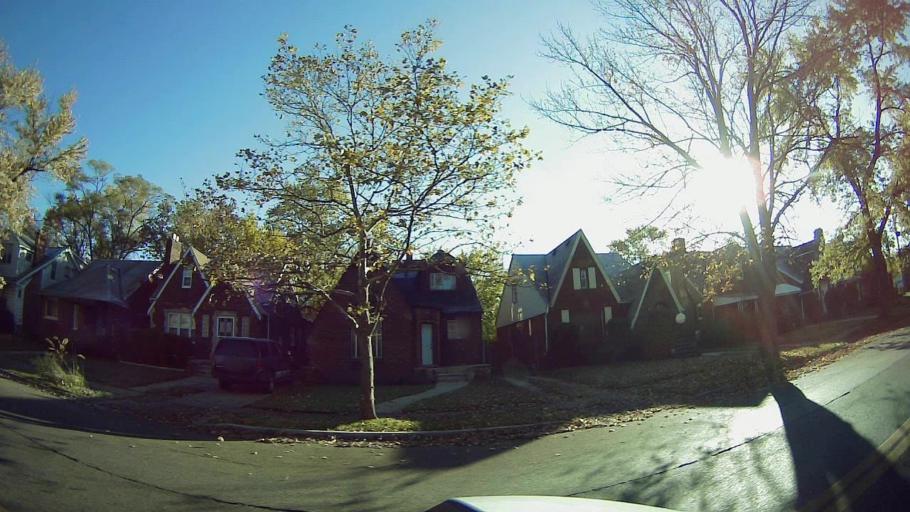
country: US
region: Michigan
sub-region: Wayne County
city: Dearborn
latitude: 42.3617
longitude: -83.1678
